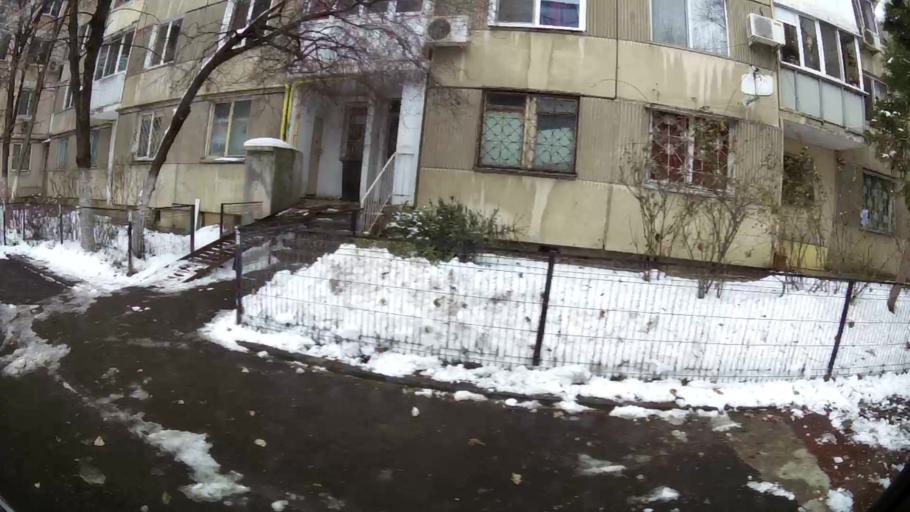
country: RO
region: Bucuresti
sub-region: Municipiul Bucuresti
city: Bucuresti
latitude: 44.3844
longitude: 26.1174
